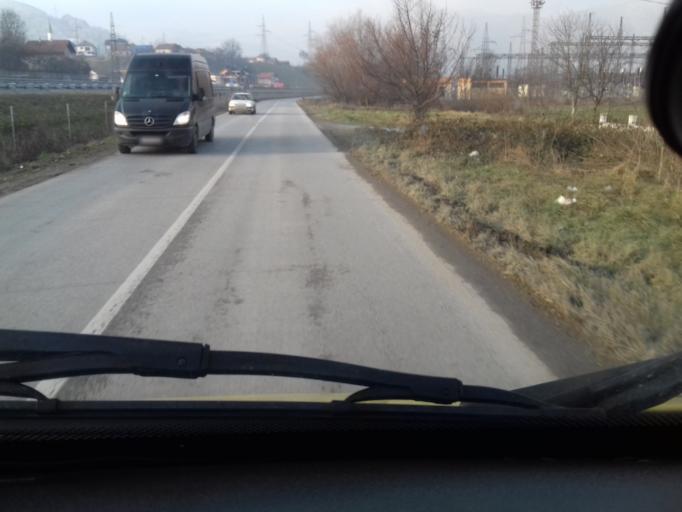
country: BA
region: Federation of Bosnia and Herzegovina
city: Dobrinje
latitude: 44.0348
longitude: 18.1235
